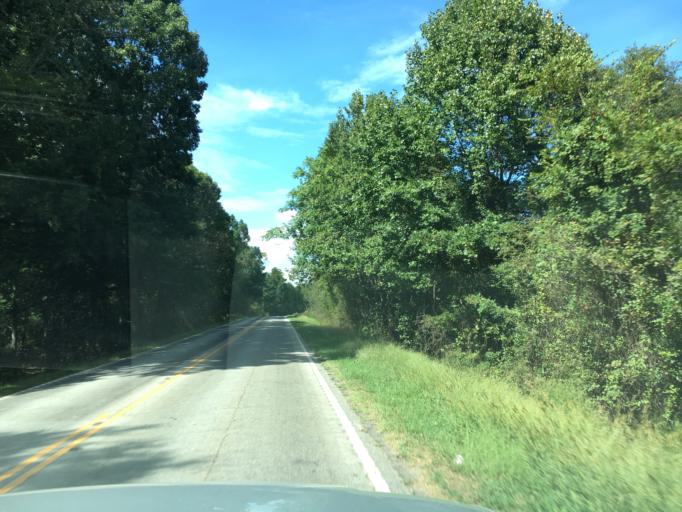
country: US
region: South Carolina
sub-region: Spartanburg County
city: Inman Mills
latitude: 34.9994
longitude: -82.1121
